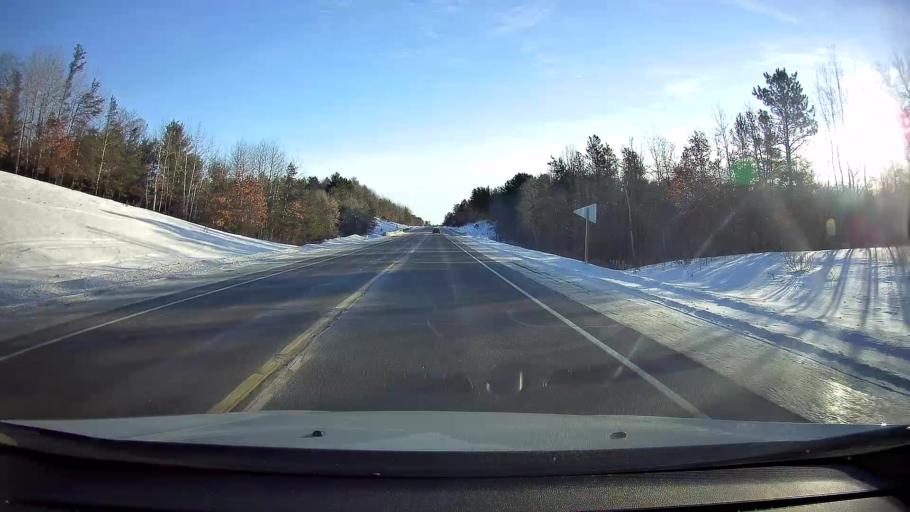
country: US
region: Wisconsin
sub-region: Washburn County
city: Spooner
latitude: 45.9104
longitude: -91.7833
